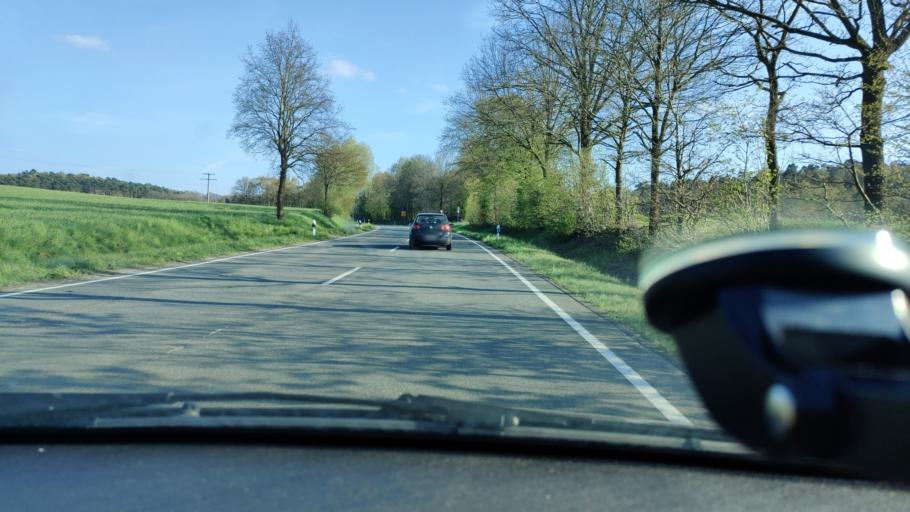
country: DE
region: North Rhine-Westphalia
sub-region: Regierungsbezirk Munster
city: Klein Reken
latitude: 51.8424
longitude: 7.0535
